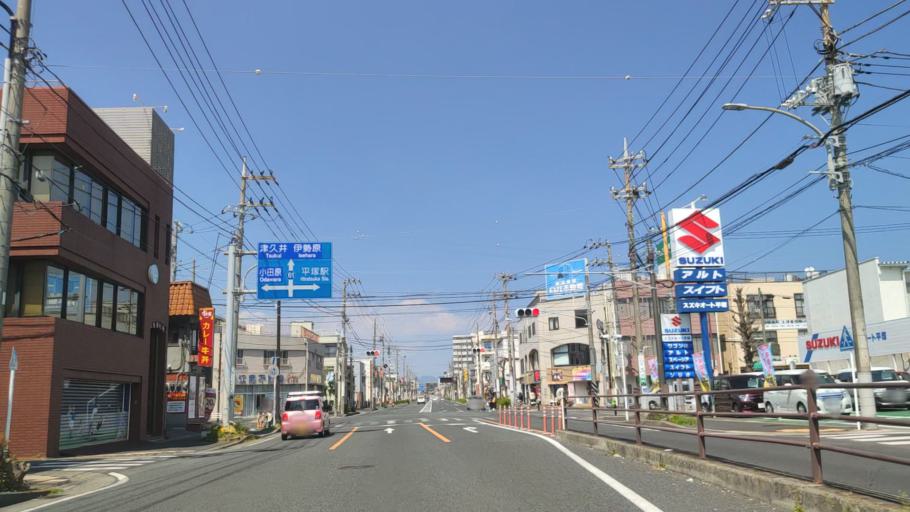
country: JP
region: Kanagawa
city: Hiratsuka
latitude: 35.3277
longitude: 139.3411
